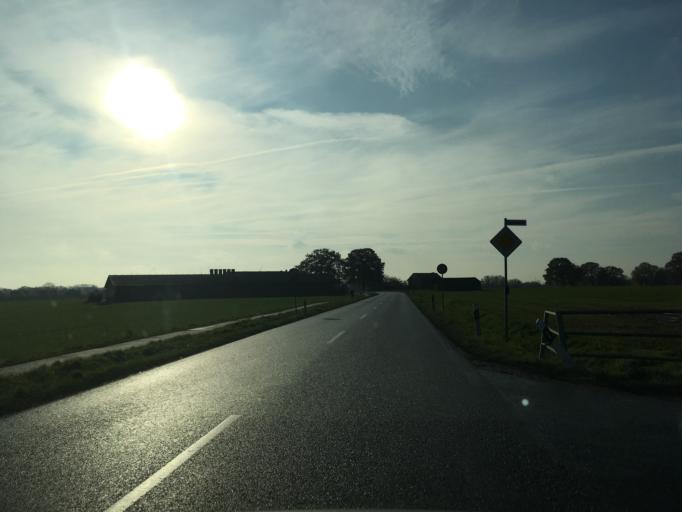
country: DE
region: North Rhine-Westphalia
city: Stadtlohn
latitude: 52.0040
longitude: 6.9370
